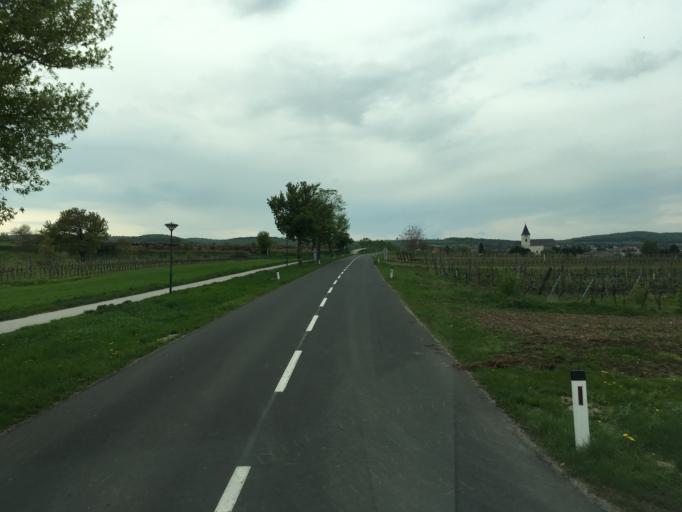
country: AT
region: Burgenland
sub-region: Eisenstadt-Umgebung
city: Breitenbrunn
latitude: 47.9378
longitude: 16.7389
